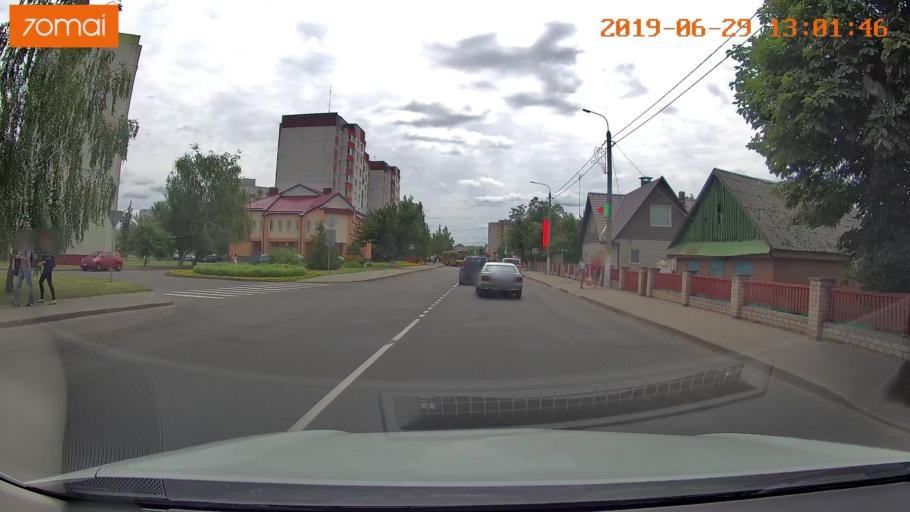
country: BY
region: Minsk
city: Slutsk
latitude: 53.0371
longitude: 27.5597
